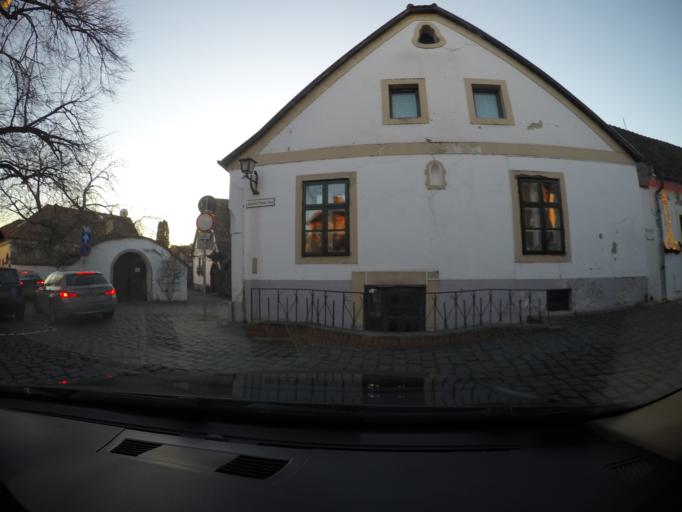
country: HU
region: Pest
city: Szentendre
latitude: 47.6671
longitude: 19.0754
